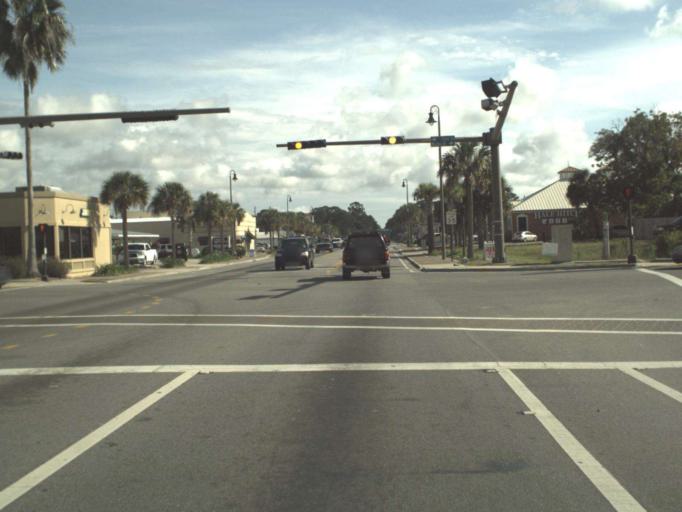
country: US
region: Florida
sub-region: Gulf County
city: Port Saint Joe
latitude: 29.8161
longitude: -85.3051
